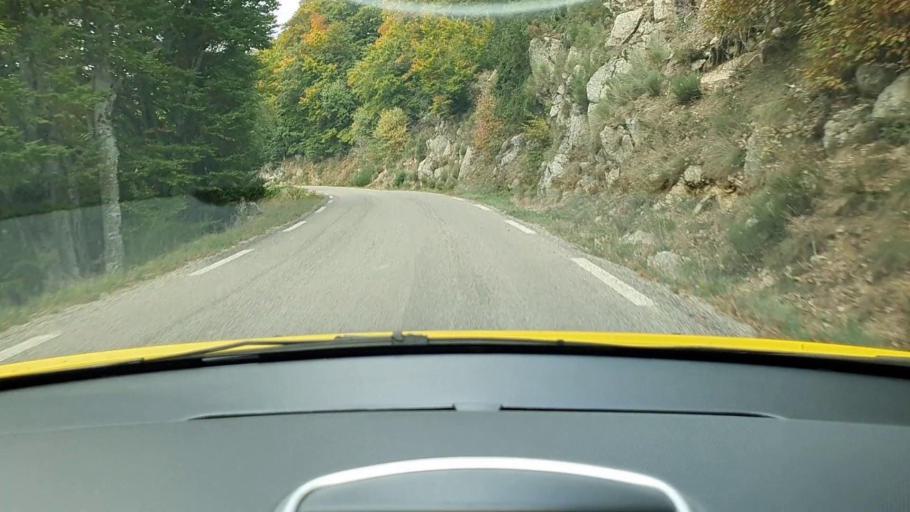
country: FR
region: Languedoc-Roussillon
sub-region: Departement du Gard
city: Le Vigan
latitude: 44.0449
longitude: 3.5571
